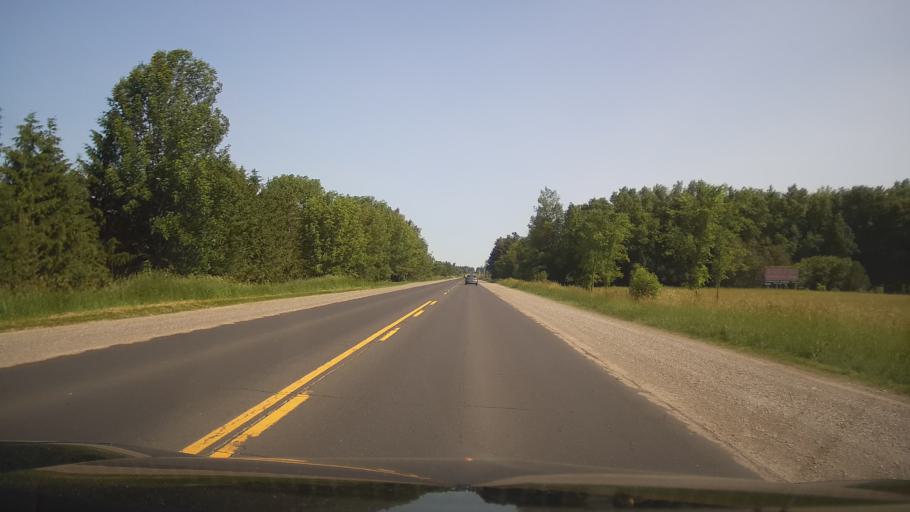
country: CA
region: Ontario
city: Omemee
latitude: 44.3169
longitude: -78.6812
